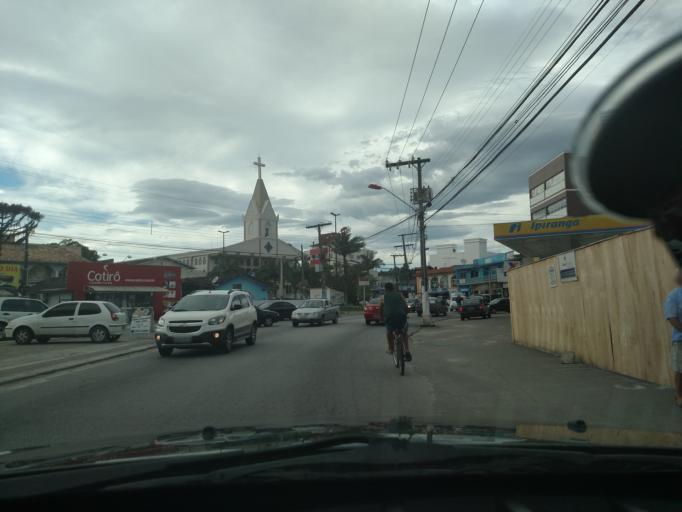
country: BR
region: Santa Catarina
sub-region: Sao Jose
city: Campinas
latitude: -27.5996
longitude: -48.6418
